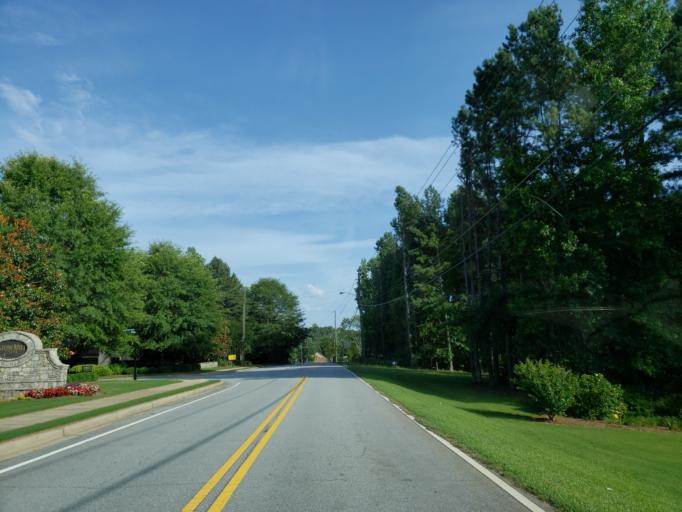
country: US
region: Georgia
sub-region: Paulding County
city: Hiram
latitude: 33.9150
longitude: -84.7177
